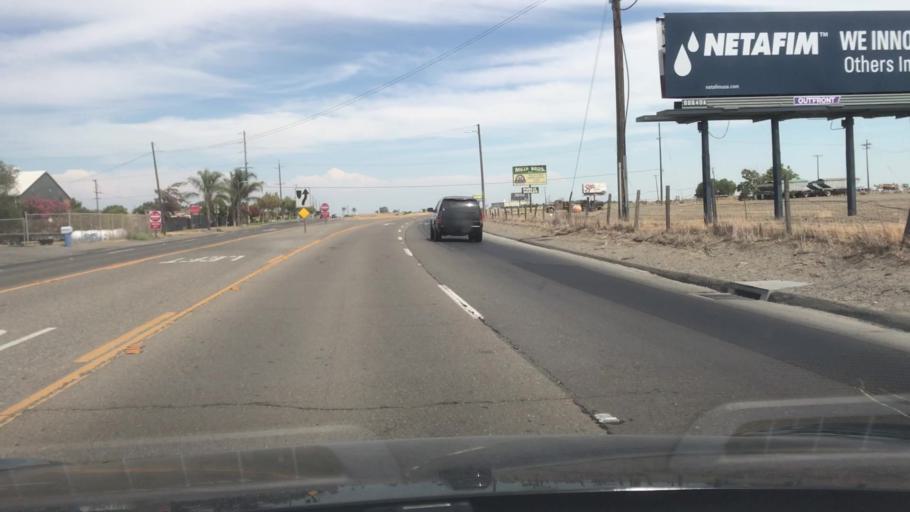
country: US
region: California
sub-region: Merced County
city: Los Banos
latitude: 37.0565
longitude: -120.8106
